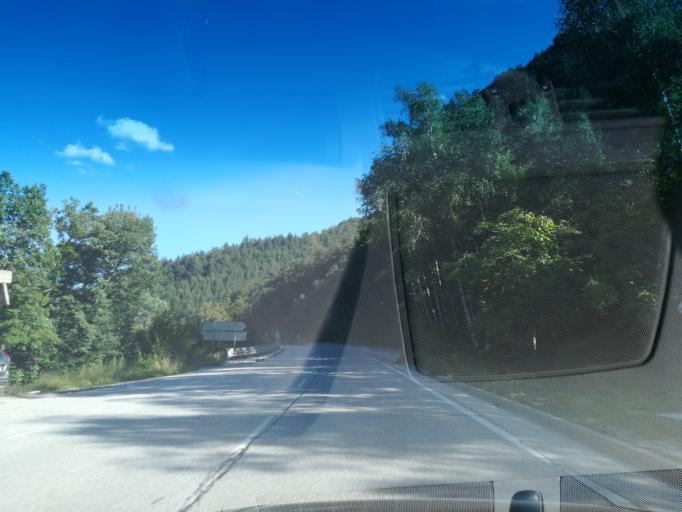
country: BG
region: Smolyan
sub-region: Obshtina Chepelare
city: Chepelare
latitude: 41.8291
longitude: 24.6860
